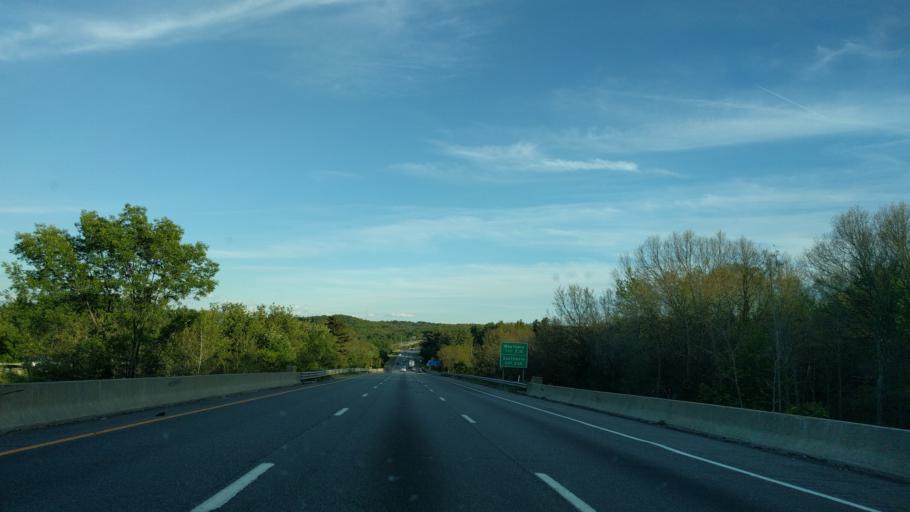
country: US
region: Massachusetts
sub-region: Middlesex County
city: Marlborough
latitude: 42.3155
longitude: -71.5691
